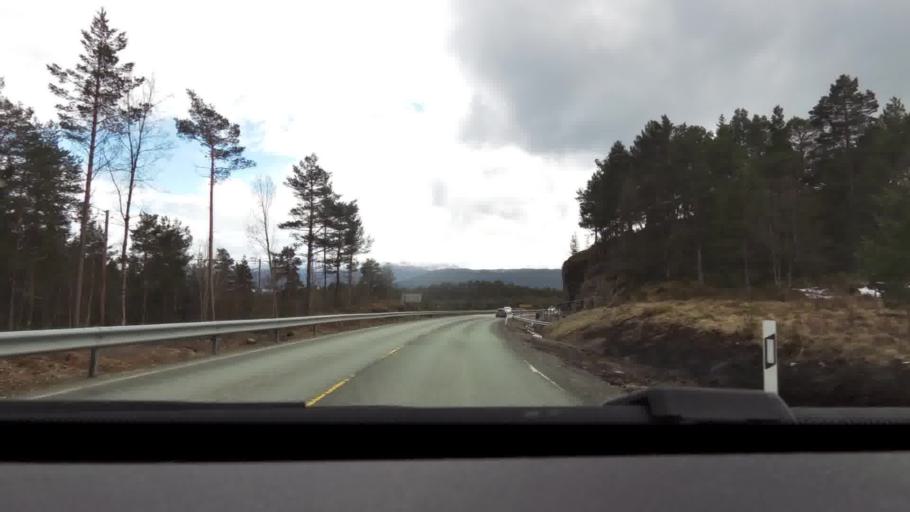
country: NO
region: More og Romsdal
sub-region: Kristiansund
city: Rensvik
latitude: 63.0424
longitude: 7.7873
